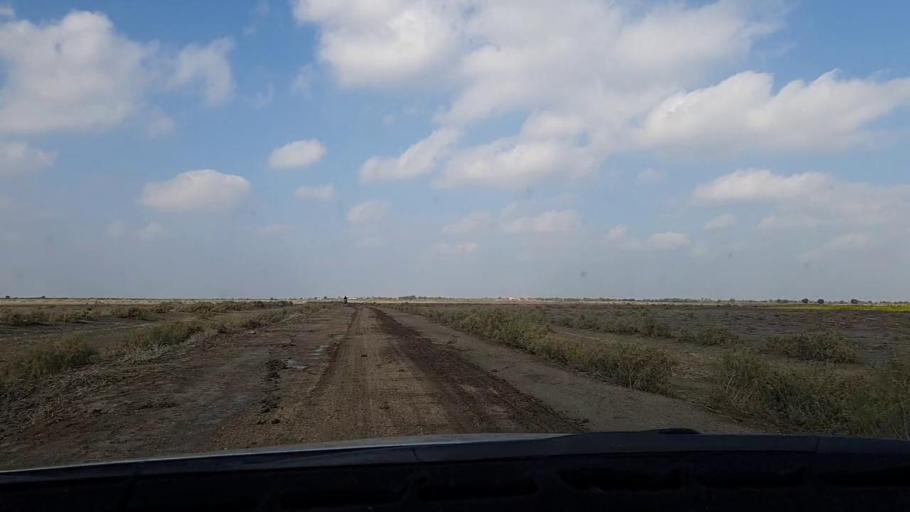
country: PK
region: Sindh
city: Tando Mittha Khan
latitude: 25.7853
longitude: 69.2560
